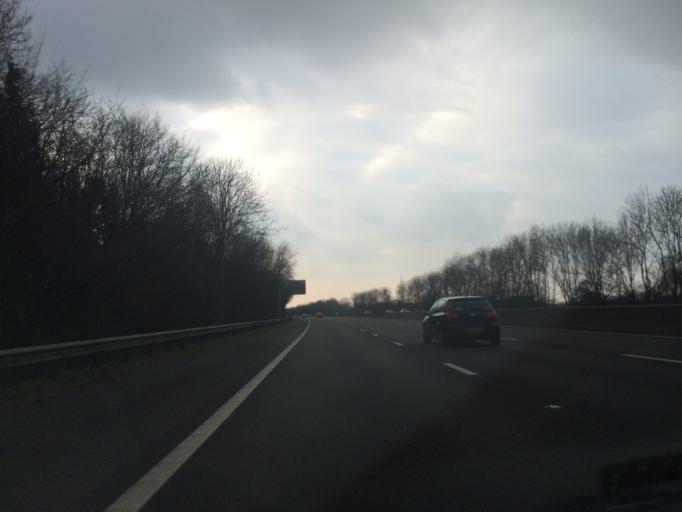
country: GB
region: England
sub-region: Wiltshire
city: Chilton Foliat
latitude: 51.4666
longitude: -1.5123
